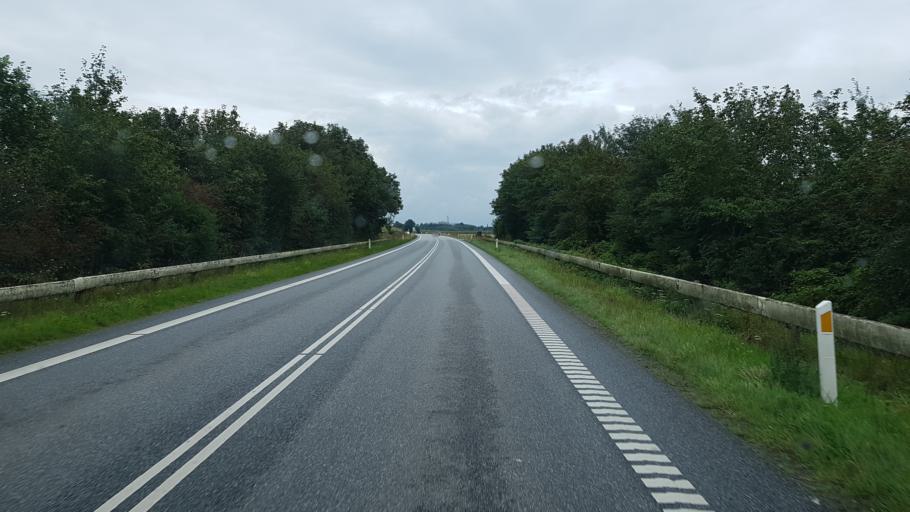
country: DK
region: Central Jutland
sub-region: Horsens Kommune
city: Braedstrup
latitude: 55.9219
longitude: 9.6844
